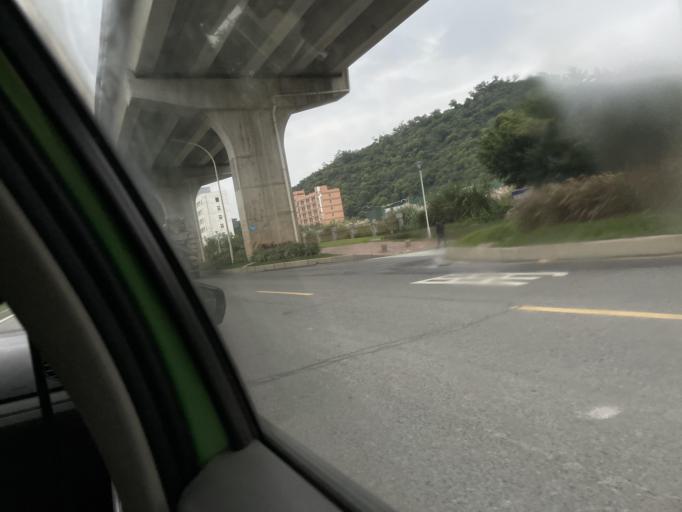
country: CN
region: Guangdong
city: Nanping
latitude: 22.1765
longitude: 113.4826
